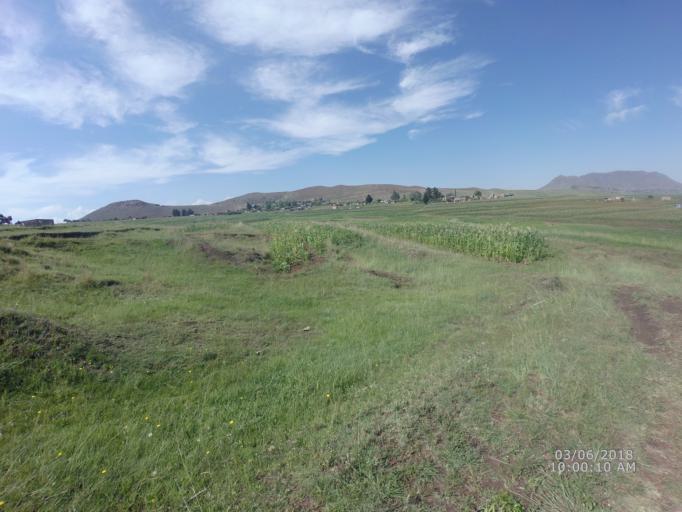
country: LS
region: Berea
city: Teyateyaneng
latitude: -29.2238
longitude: 27.8668
